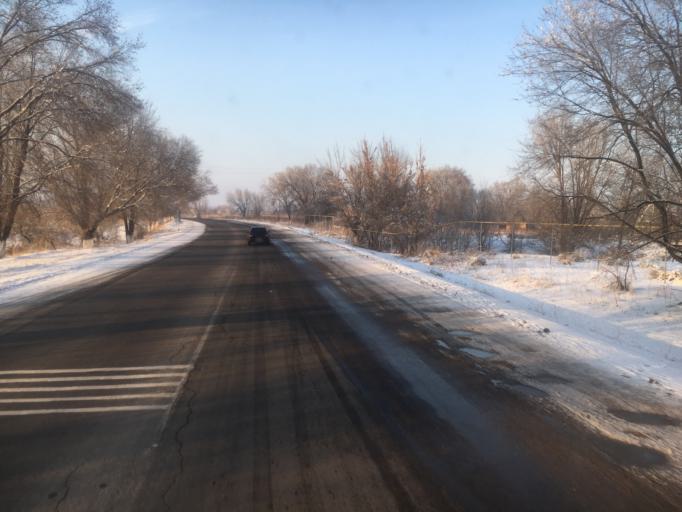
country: KZ
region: Almaty Oblysy
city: Burunday
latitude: 43.3400
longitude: 76.6588
